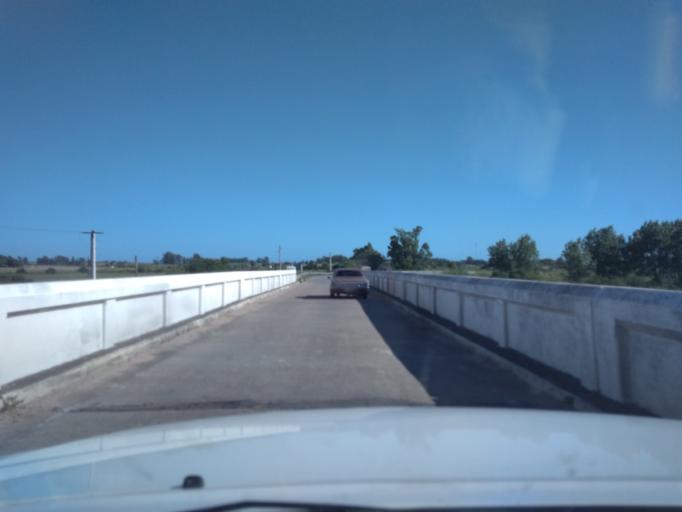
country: UY
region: Canelones
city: San Ramon
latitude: -34.3233
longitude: -55.9615
